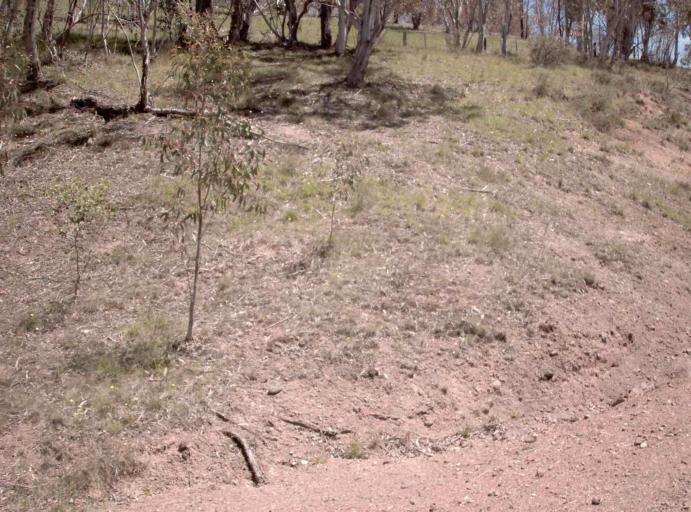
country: AU
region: New South Wales
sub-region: Snowy River
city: Jindabyne
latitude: -37.0657
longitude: 148.2614
